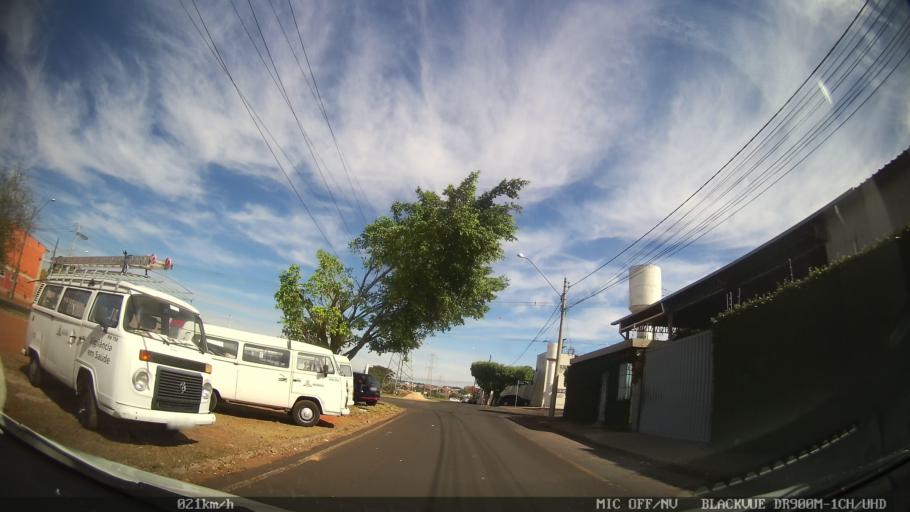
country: BR
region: Sao Paulo
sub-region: Sao Jose Do Rio Preto
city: Sao Jose do Rio Preto
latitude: -20.8368
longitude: -49.3545
